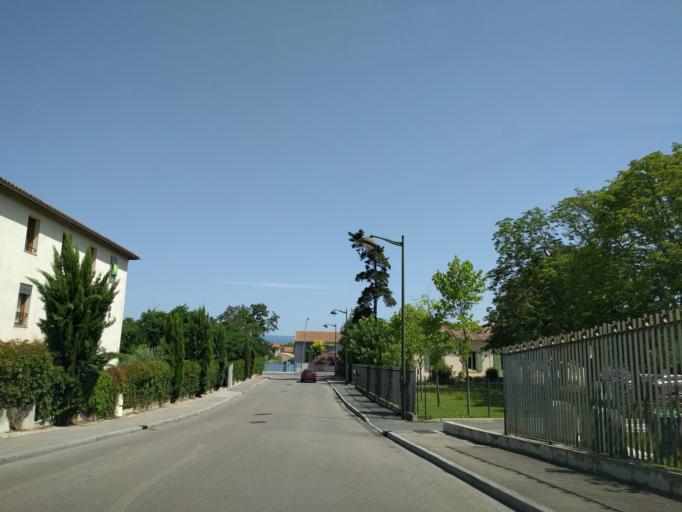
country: FR
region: Languedoc-Roussillon
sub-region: Departement de l'Aude
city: Carcassonne
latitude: 43.2072
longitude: 2.3728
